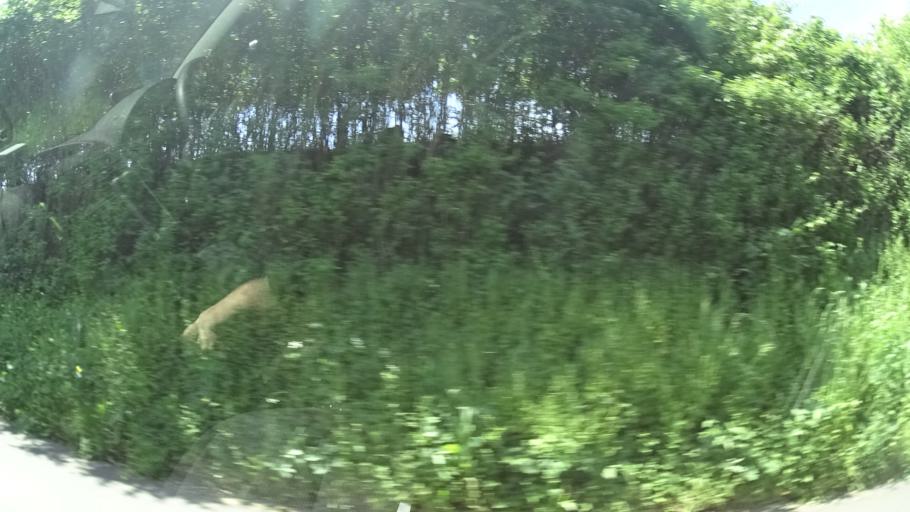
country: DE
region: Bavaria
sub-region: Regierungsbezirk Unterfranken
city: Poppenhausen
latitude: 50.0904
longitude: 10.1427
